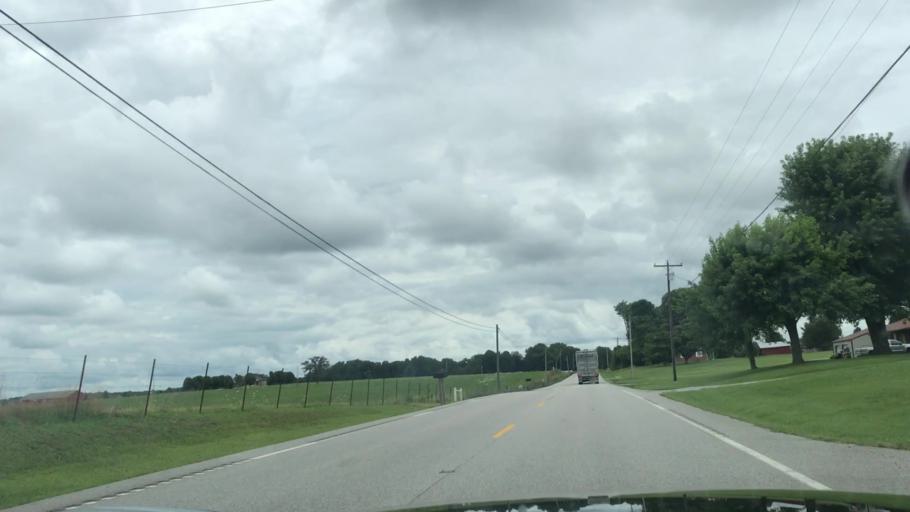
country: US
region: Tennessee
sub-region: Fentress County
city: Jamestown
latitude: 36.3587
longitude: -84.8264
